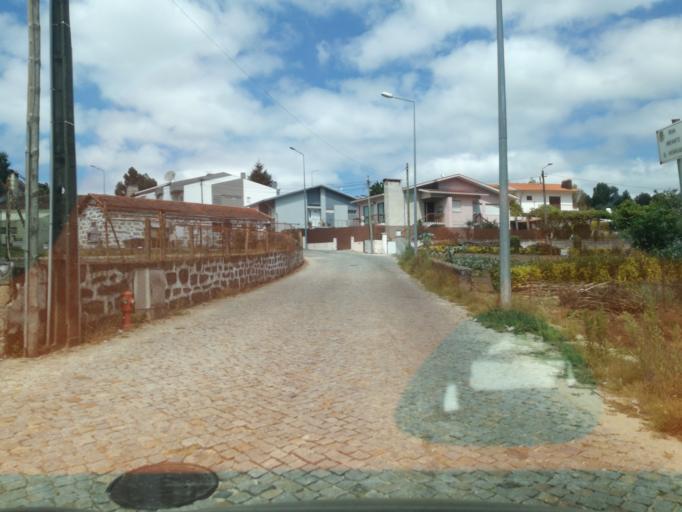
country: PT
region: Porto
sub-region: Maia
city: Nogueira
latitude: 41.2412
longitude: -8.5965
